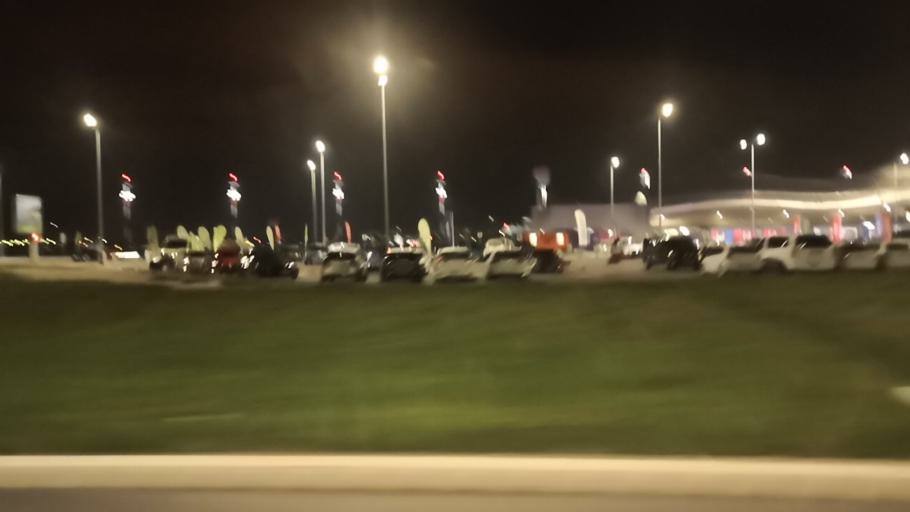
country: HR
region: Zagrebacka
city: Micevec
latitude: 45.7385
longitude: 16.0798
